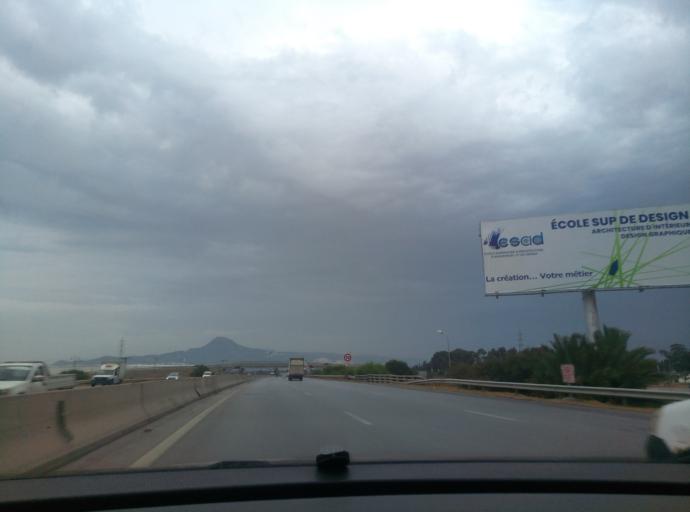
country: TN
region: Bin 'Arus
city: Ben Arous
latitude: 36.7269
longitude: 10.2507
